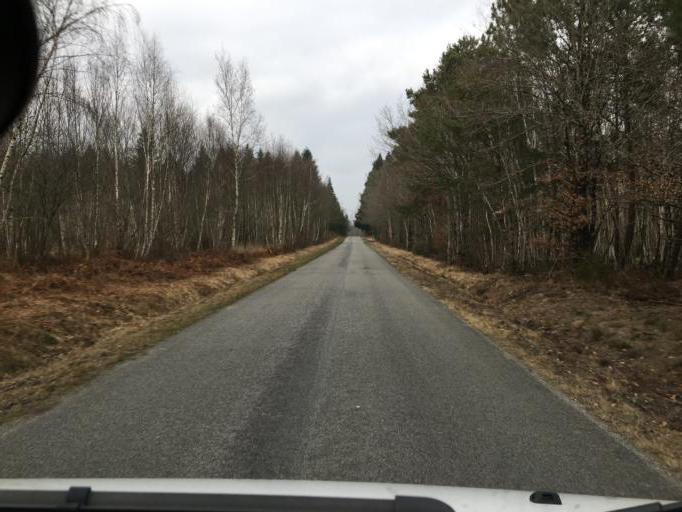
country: FR
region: Centre
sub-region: Departement du Loir-et-Cher
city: Neung-sur-Beuvron
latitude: 47.4744
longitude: 1.7353
